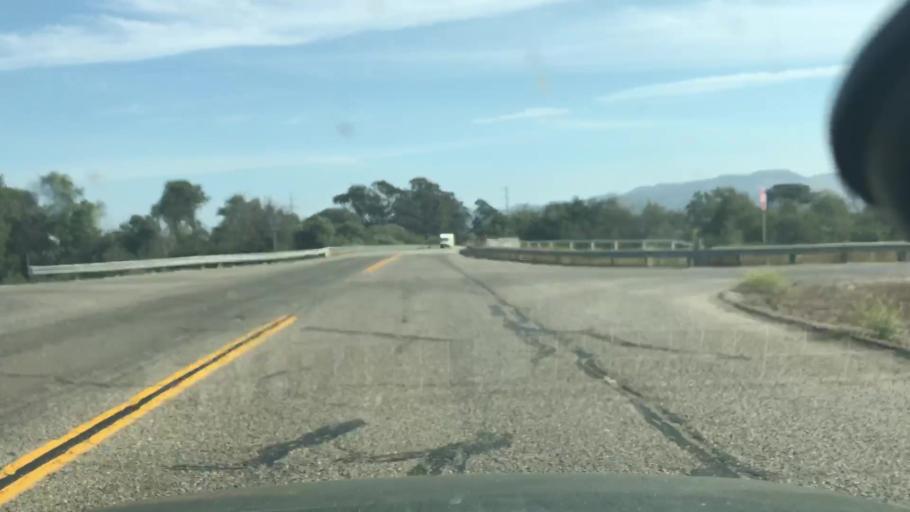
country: US
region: California
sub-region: Santa Barbara County
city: Vandenberg Village
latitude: 34.6734
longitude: -120.4936
